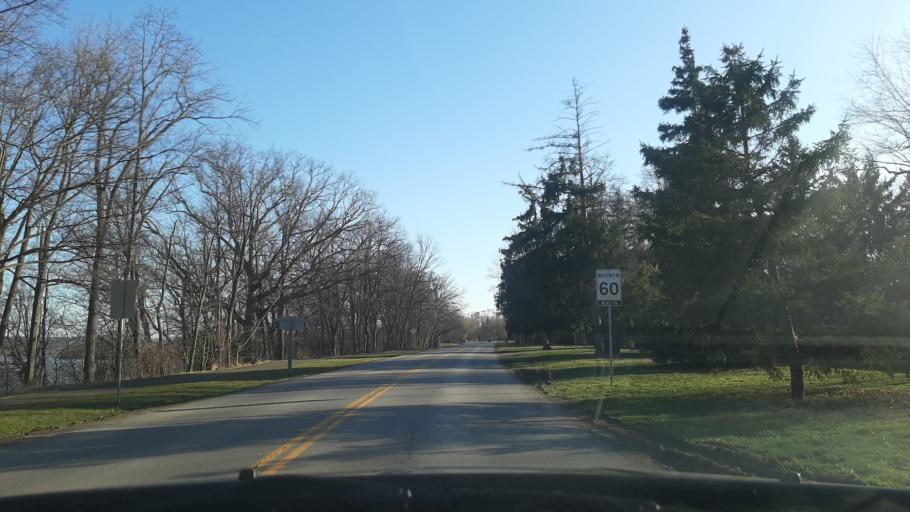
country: US
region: New York
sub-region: Niagara County
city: Youngstown
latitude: 43.2190
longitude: -79.0594
